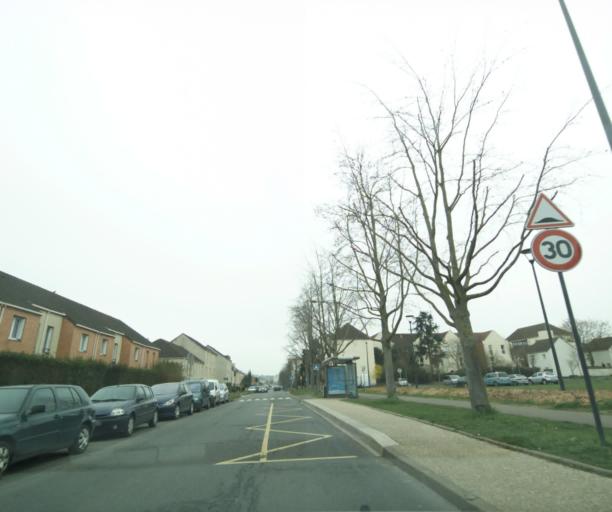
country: FR
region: Ile-de-France
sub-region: Departement du Val-d'Oise
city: Courdimanche
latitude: 49.0499
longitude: 2.0179
